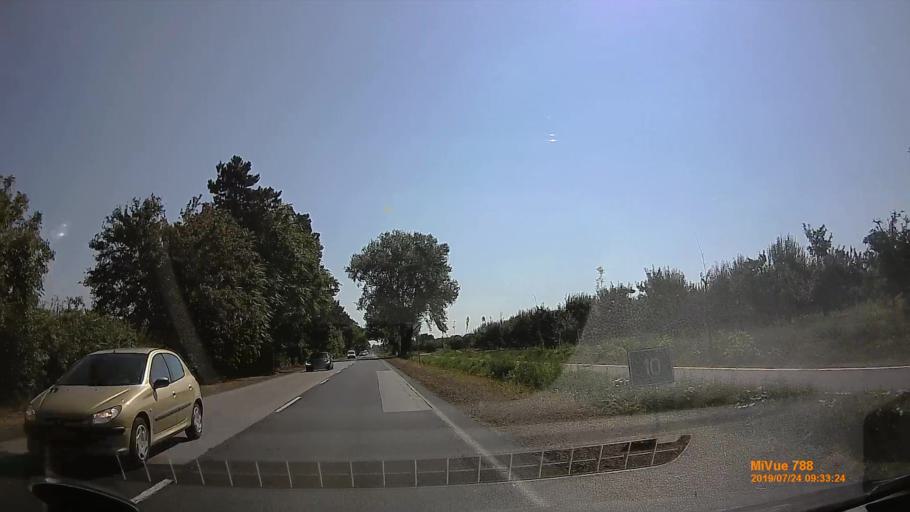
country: HU
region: Szabolcs-Szatmar-Bereg
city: Napkor
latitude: 47.9502
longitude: 21.8490
